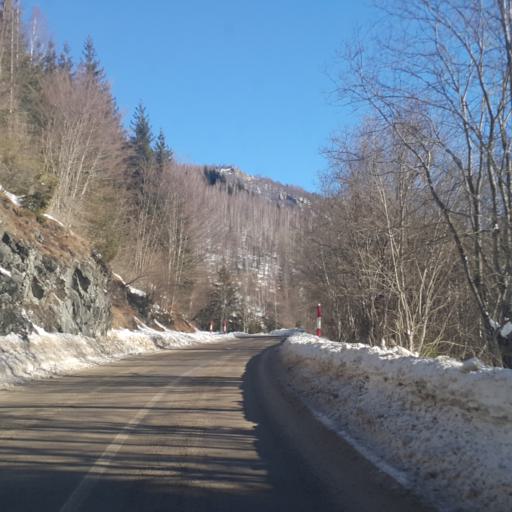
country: XK
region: Mitrovica
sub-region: Komuna e Leposaviqit
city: Leposaviq
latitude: 43.3061
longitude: 20.8591
